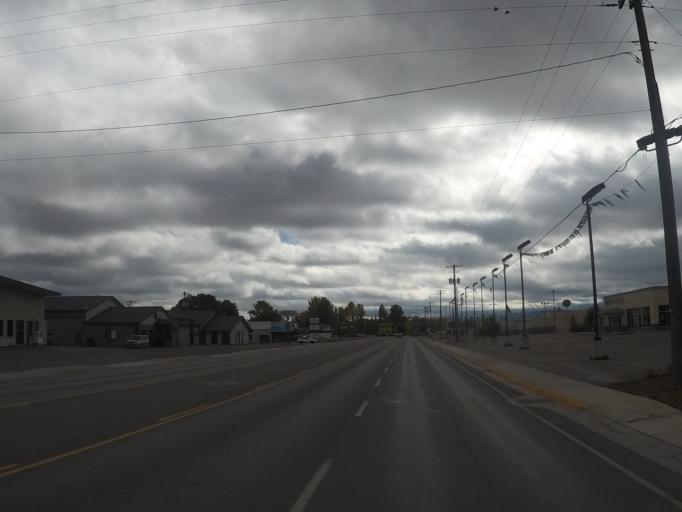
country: US
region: Montana
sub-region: Flathead County
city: Evergreen
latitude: 48.2172
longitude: -114.2773
